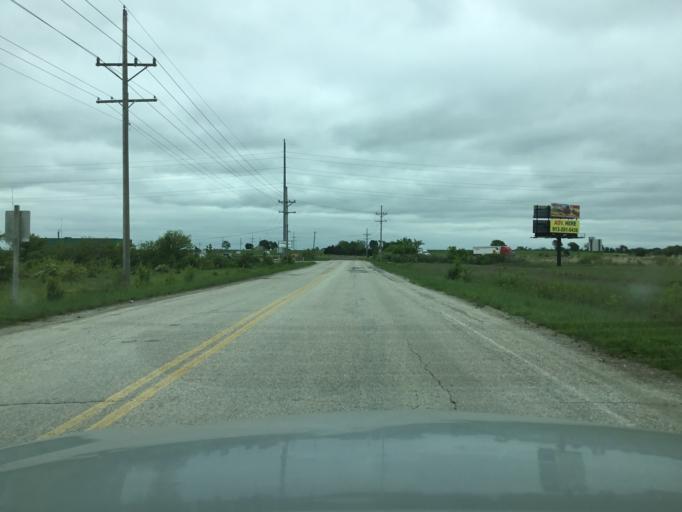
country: US
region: Kansas
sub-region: Franklin County
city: Ottawa
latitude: 38.5793
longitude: -95.2605
